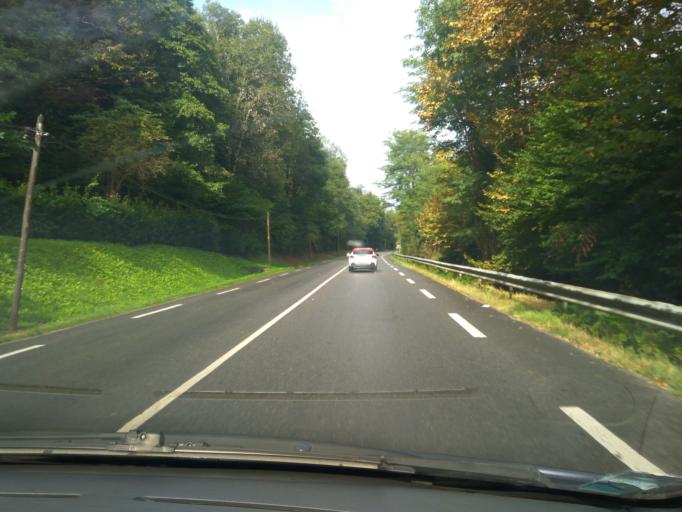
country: FR
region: Aquitaine
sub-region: Departement des Pyrenees-Atlantiques
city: Billere
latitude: 43.3026
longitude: -0.4330
